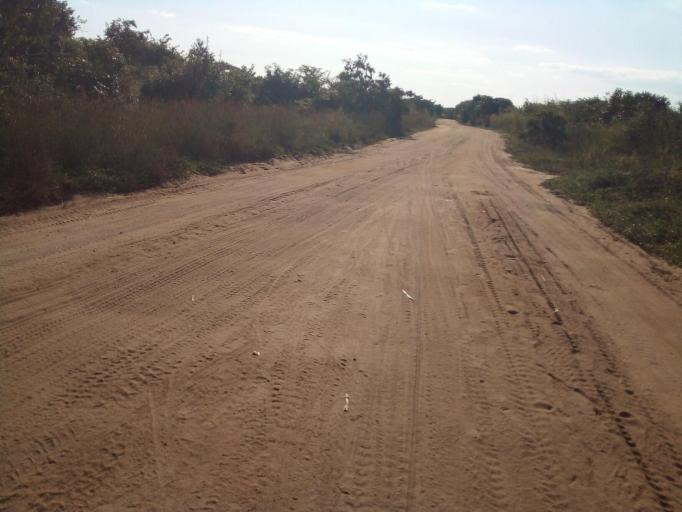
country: MZ
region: Zambezia
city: Quelimane
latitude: -17.5105
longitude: 36.8329
